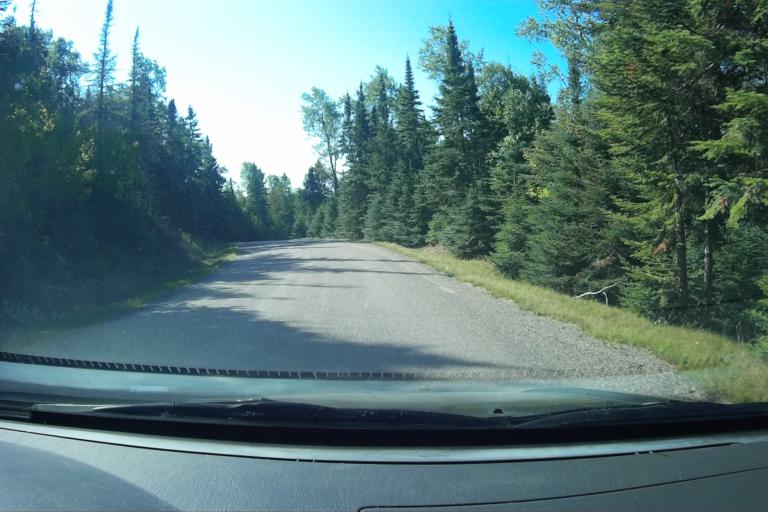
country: CA
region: Ontario
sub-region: Thunder Bay District
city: Thunder Bay
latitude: 48.3392
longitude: -88.8232
